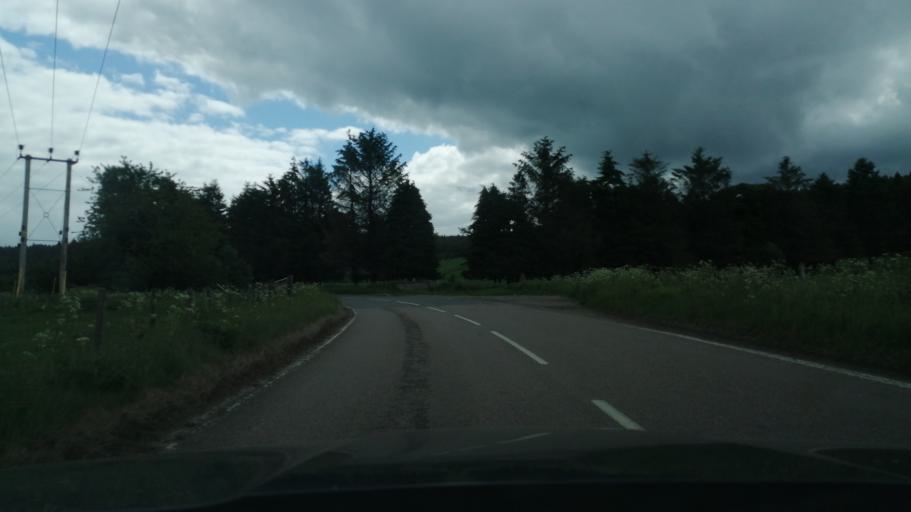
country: GB
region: Scotland
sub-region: Moray
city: Fochabers
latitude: 57.5468
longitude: -3.1240
